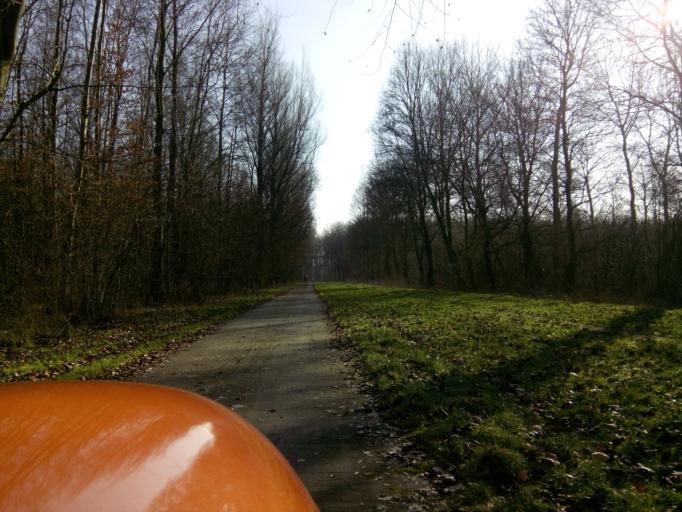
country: NL
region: Flevoland
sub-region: Gemeente Zeewolde
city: Zeewolde
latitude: 52.2953
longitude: 5.5038
